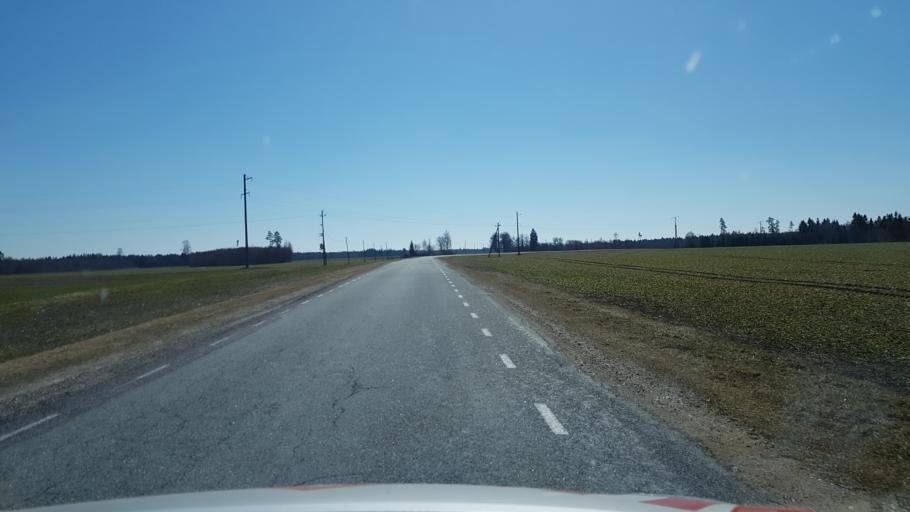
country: EE
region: Laeaene-Virumaa
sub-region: Rakke vald
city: Rakke
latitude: 59.0251
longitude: 26.3519
